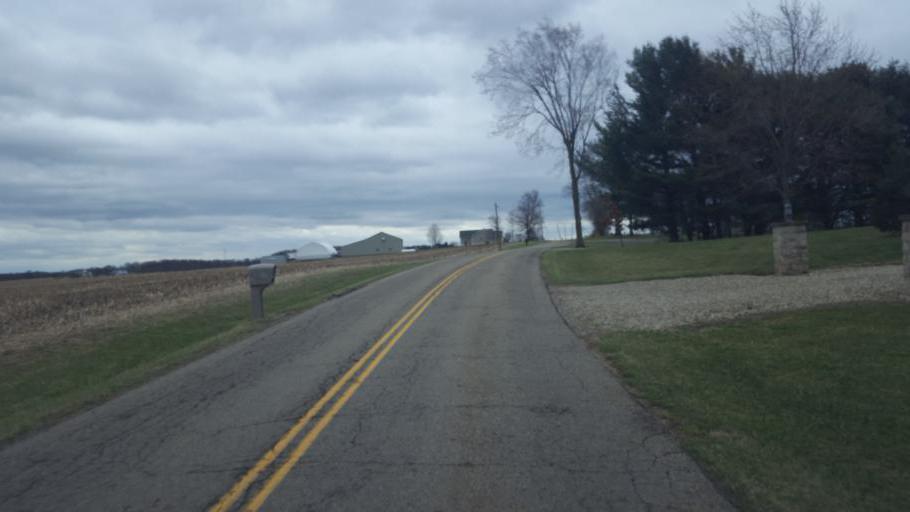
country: US
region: Ohio
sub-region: Knox County
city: Fredericktown
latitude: 40.4257
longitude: -82.6220
